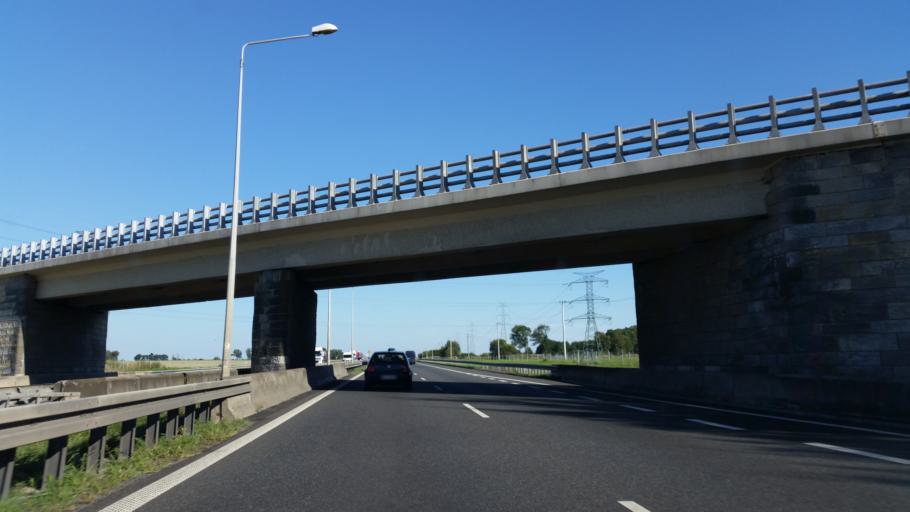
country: PL
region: Opole Voivodeship
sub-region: Powiat brzeski
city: Olszanka
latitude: 50.7637
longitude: 17.4159
